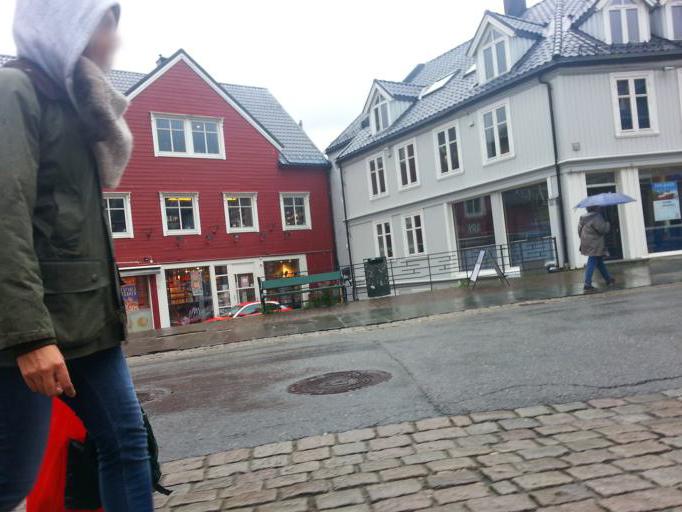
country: NO
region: Troms
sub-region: Tromso
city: Tromso
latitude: 69.6505
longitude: 18.9567
